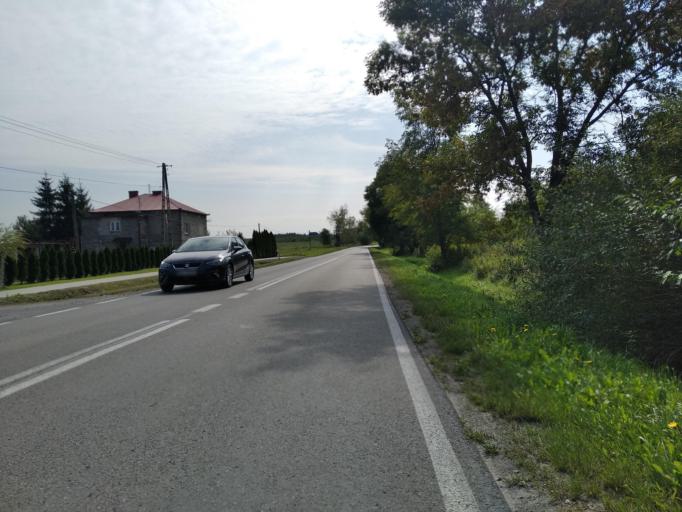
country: PL
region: Subcarpathian Voivodeship
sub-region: Powiat ropczycko-sedziszowski
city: Ostrow
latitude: 50.1111
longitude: 21.5919
